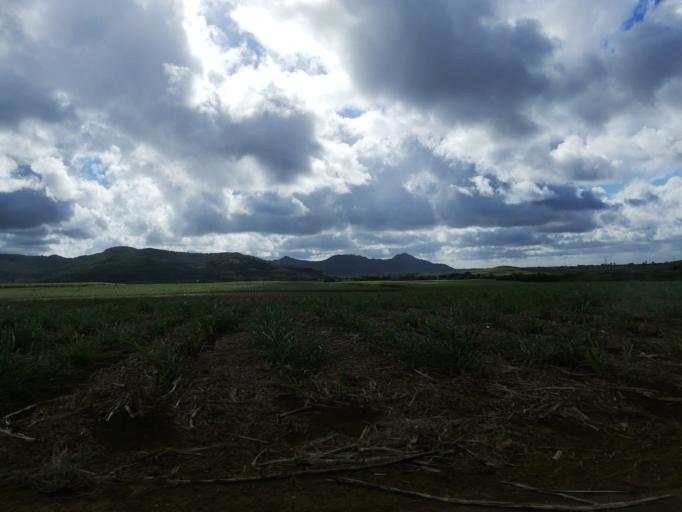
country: MU
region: Flacq
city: Grande Riviere Sud Est
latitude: -20.2823
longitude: 57.7562
